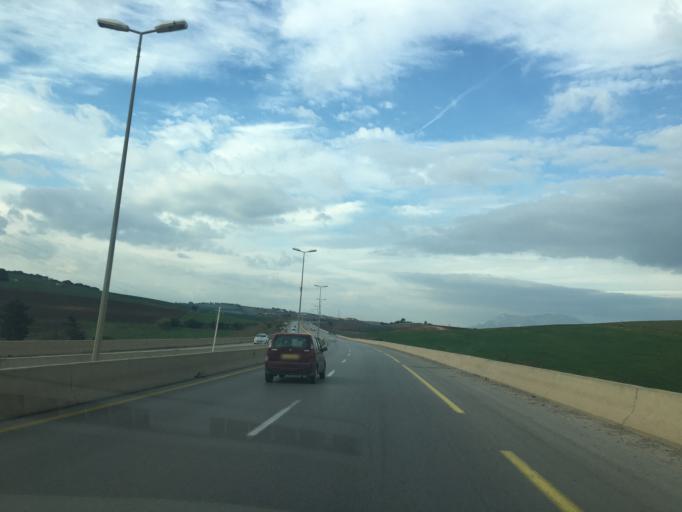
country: DZ
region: Tipaza
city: Tipasa
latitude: 36.5760
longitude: 2.5337
